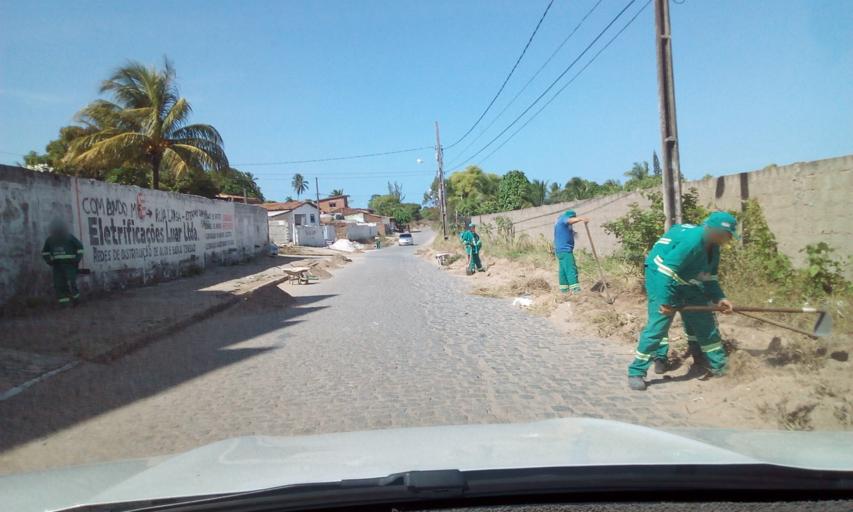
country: BR
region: Paraiba
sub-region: Joao Pessoa
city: Joao Pessoa
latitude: -7.1587
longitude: -34.8459
